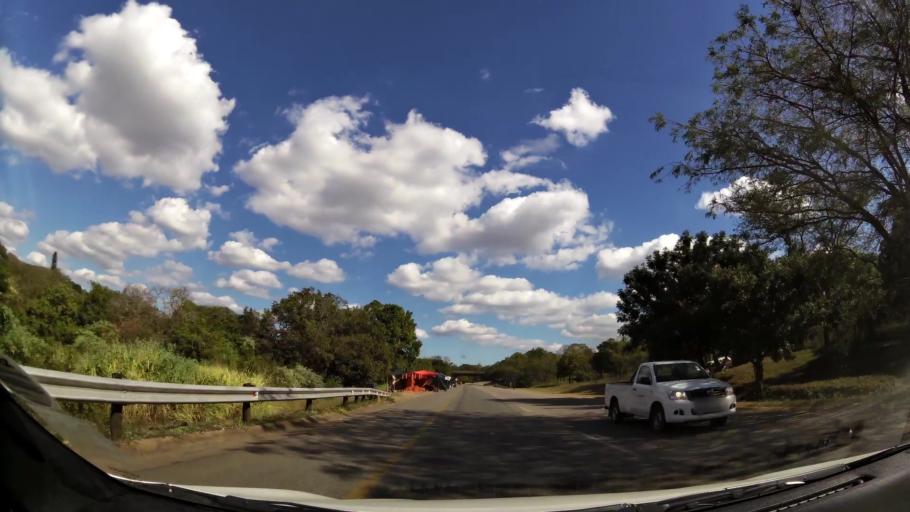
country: ZA
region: Limpopo
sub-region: Mopani District Municipality
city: Tzaneen
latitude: -23.8273
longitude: 30.1531
